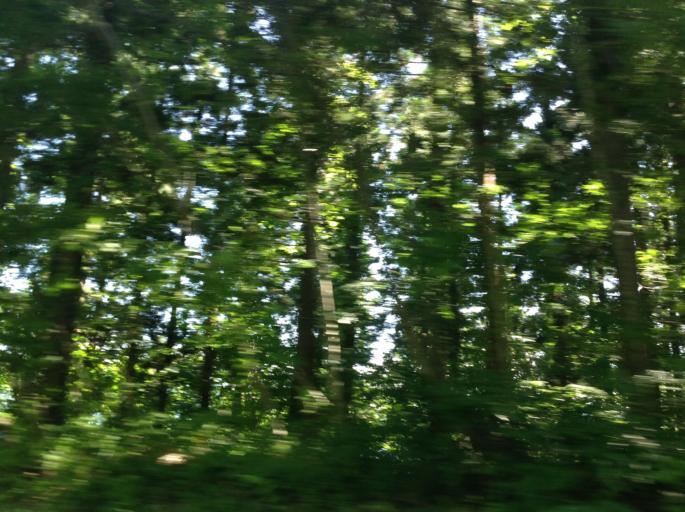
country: JP
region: Akita
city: Kakunodatemachi
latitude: 39.6980
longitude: 140.6491
